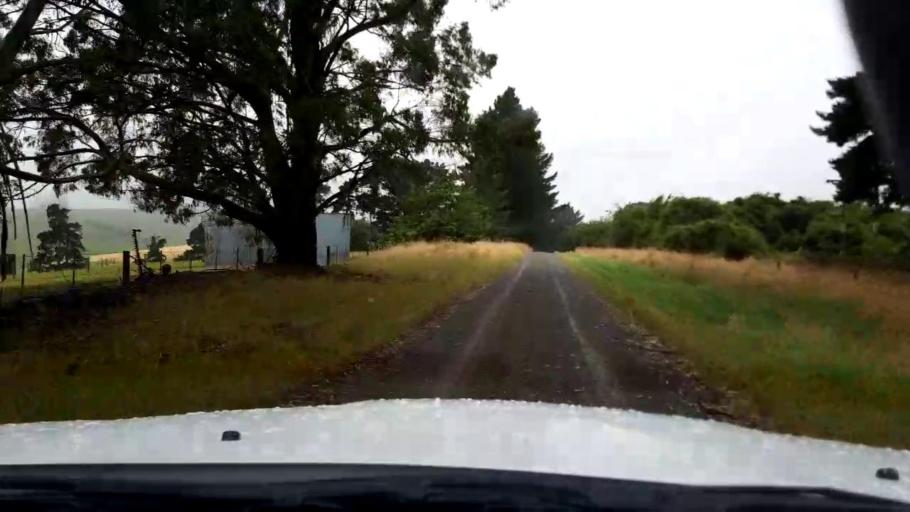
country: NZ
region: Canterbury
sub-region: Timaru District
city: Pleasant Point
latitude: -44.1780
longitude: 171.0972
